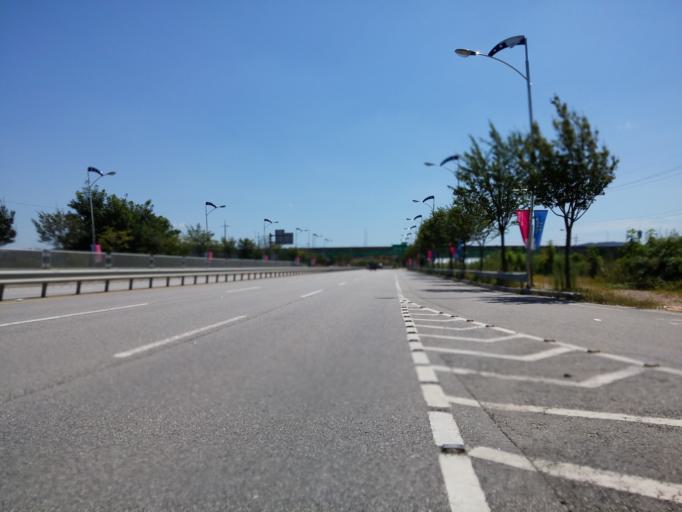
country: KR
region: Chungcheongbuk-do
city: Cheongju-si
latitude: 36.6213
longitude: 127.3398
